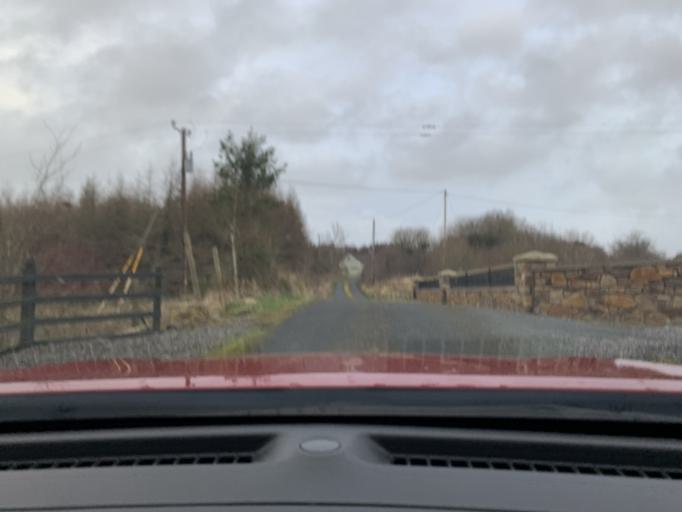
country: IE
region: Connaught
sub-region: Roscommon
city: Boyle
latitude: 53.9839
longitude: -8.4227
